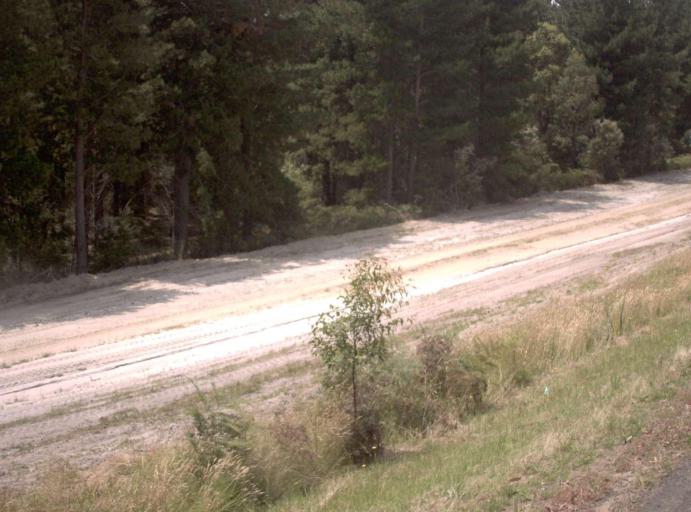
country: AU
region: Victoria
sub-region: Latrobe
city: Traralgon
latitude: -38.2592
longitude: 146.6789
